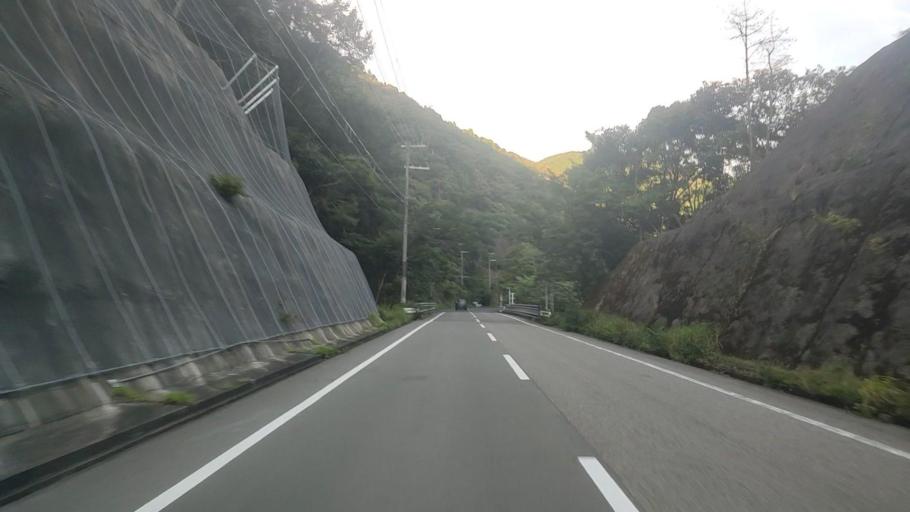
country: JP
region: Wakayama
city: Tanabe
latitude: 33.8151
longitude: 135.5705
